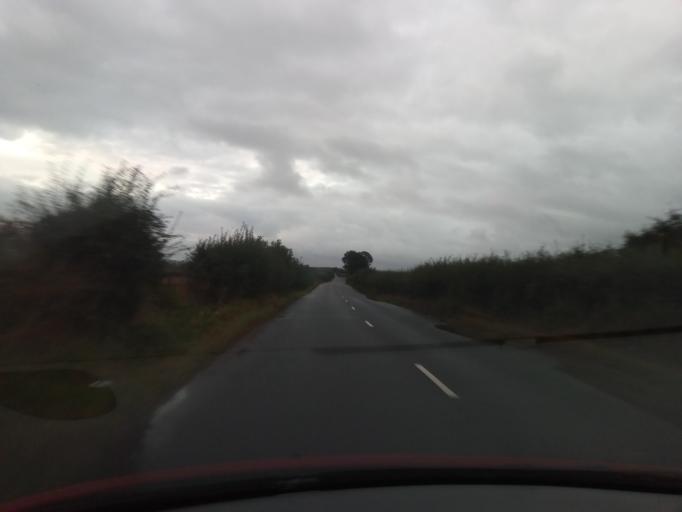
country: GB
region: England
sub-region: Darlington
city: Denton
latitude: 54.5546
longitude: -1.6751
